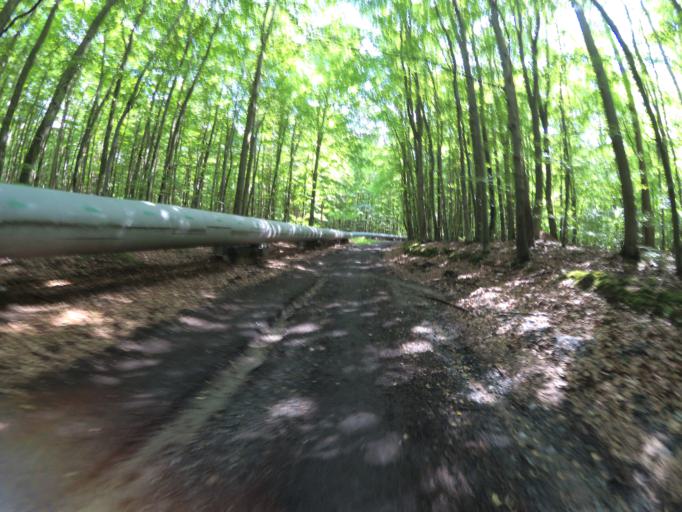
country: PL
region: Pomeranian Voivodeship
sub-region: Gdynia
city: Wielki Kack
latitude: 54.5065
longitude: 18.4909
